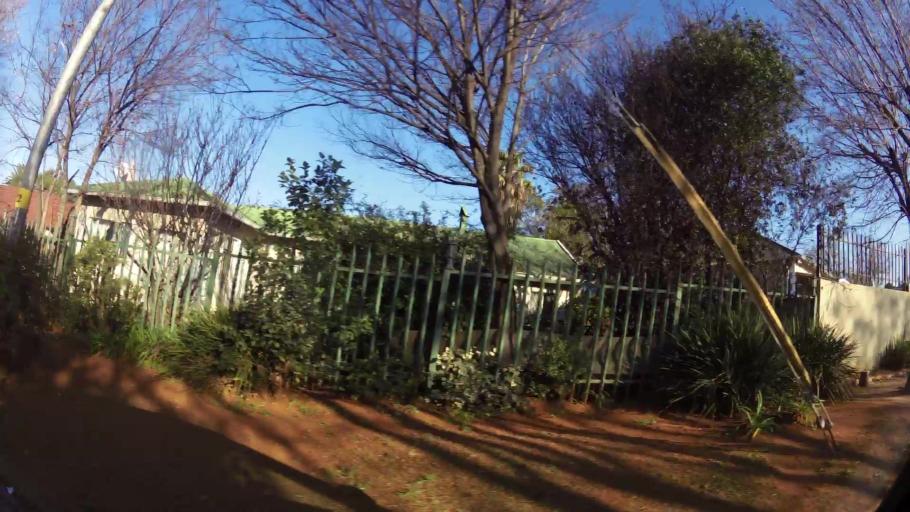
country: ZA
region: Gauteng
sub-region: Ekurhuleni Metropolitan Municipality
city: Germiston
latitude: -26.1947
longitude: 28.1471
